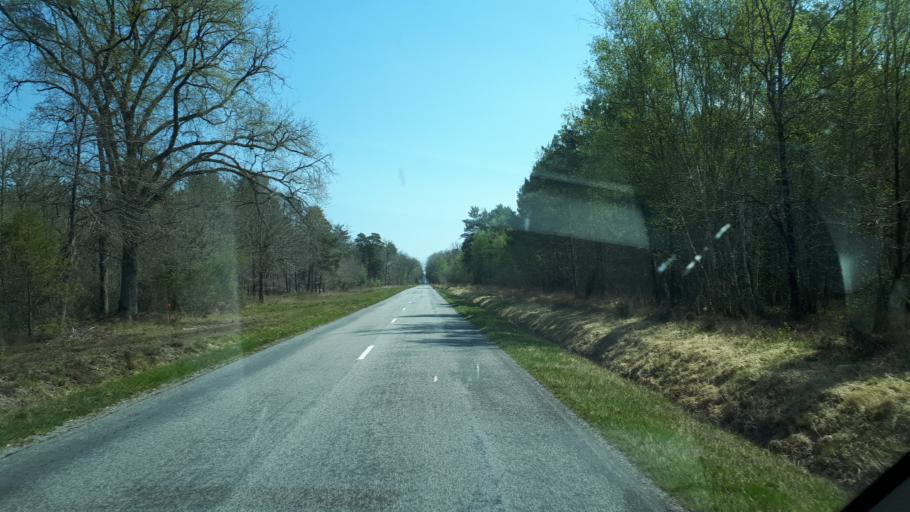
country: FR
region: Centre
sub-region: Departement du Loir-et-Cher
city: Theillay
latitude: 47.3169
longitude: 2.1356
